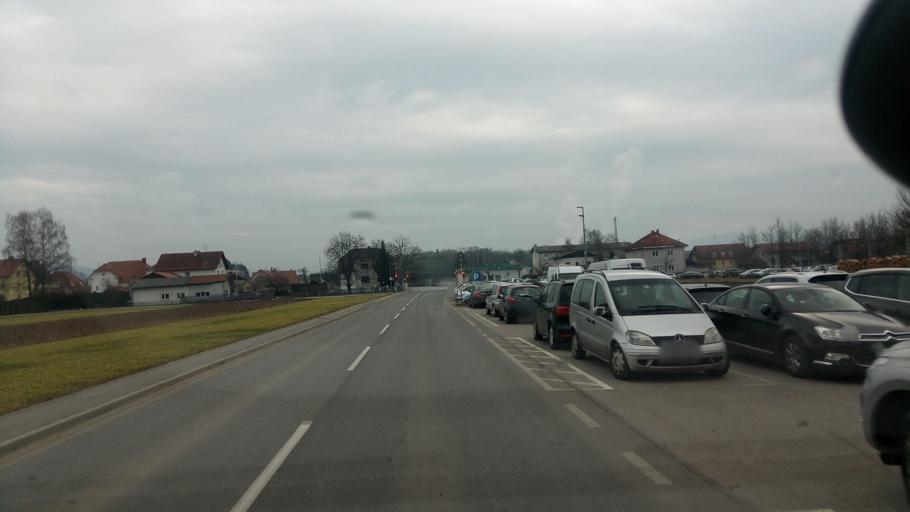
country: SI
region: Menges
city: Preserje pri Radomljah
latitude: 46.1677
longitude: 14.5920
